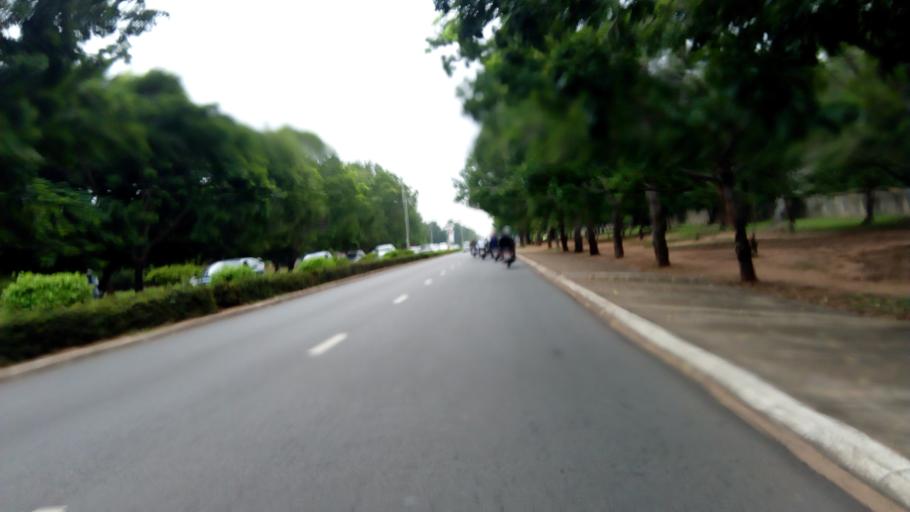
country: TG
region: Maritime
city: Lome
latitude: 6.1737
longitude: 1.2186
